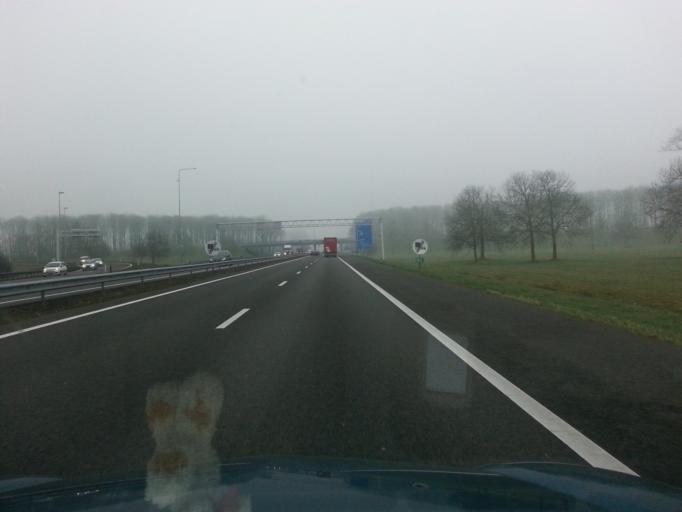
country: NL
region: Gelderland
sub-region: Gemeente Zevenaar
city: Zevenaar
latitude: 51.9156
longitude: 6.1375
